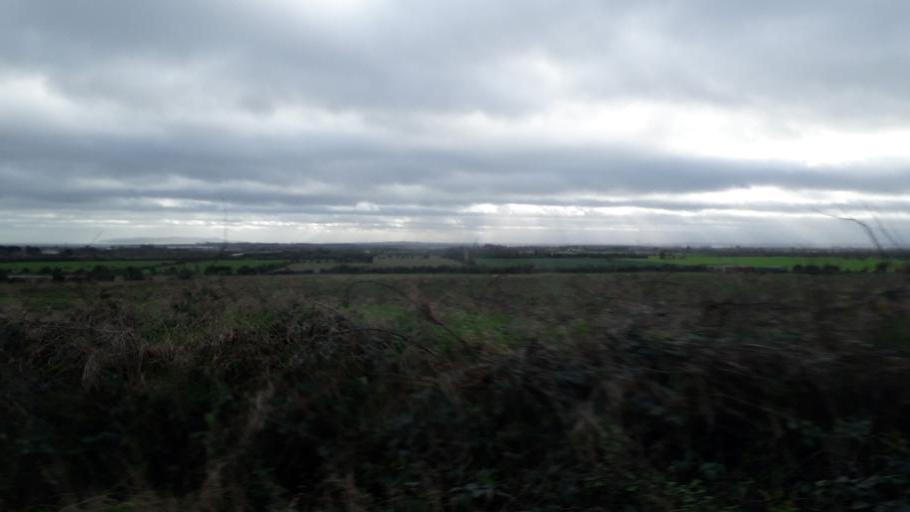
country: IE
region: Leinster
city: An Ros
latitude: 53.5512
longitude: -6.1232
